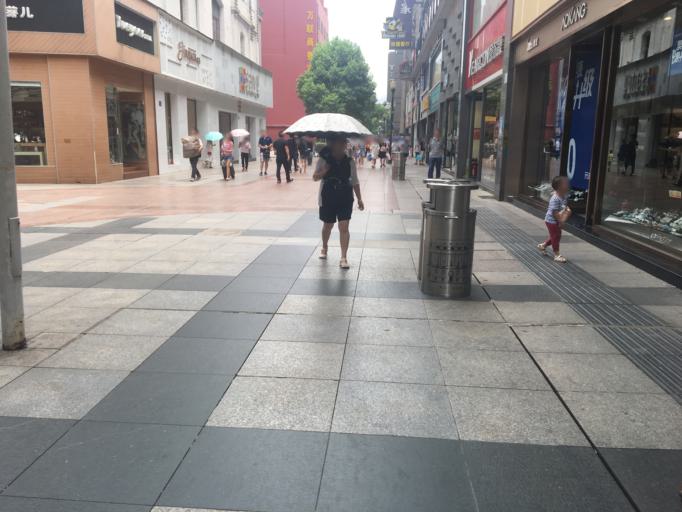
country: CN
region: Hubei
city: Wuhan
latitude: 30.5807
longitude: 114.2893
